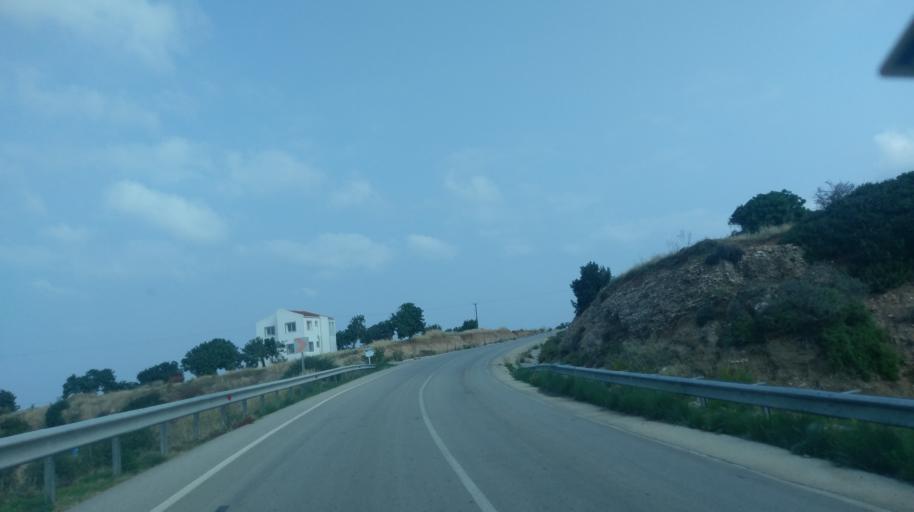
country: CY
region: Ammochostos
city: Lefkonoiko
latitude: 35.3828
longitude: 33.7208
